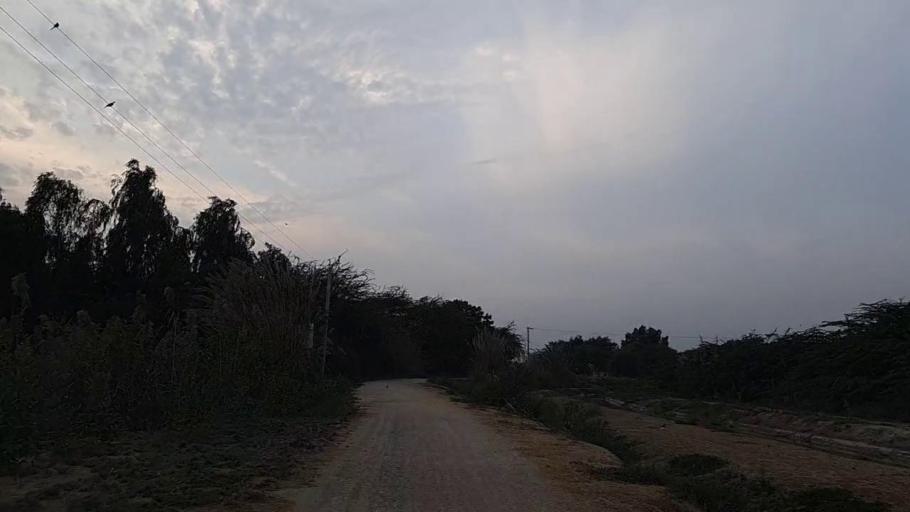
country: PK
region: Sindh
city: Thatta
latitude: 24.7689
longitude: 67.9262
